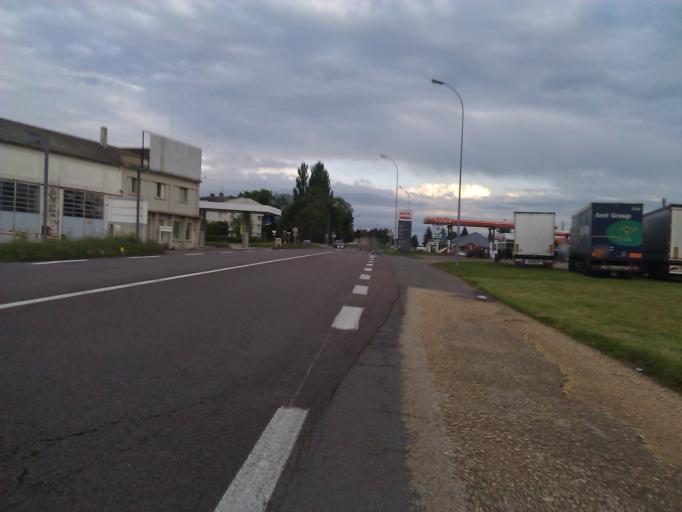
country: FR
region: Bourgogne
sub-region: Departement de Saone-et-Loire
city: Saint-Remy
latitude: 46.7551
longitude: 4.8461
